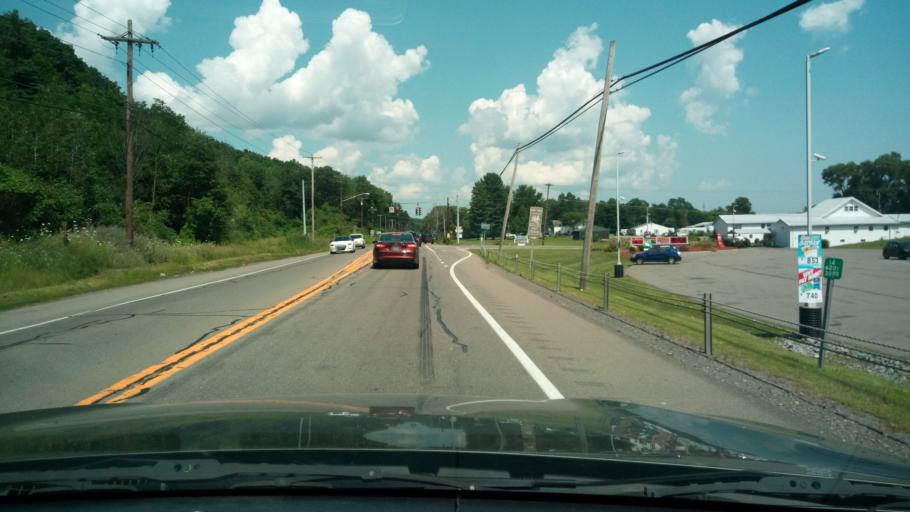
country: US
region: New York
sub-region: Chemung County
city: Horseheads
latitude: 42.1885
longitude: -76.8344
